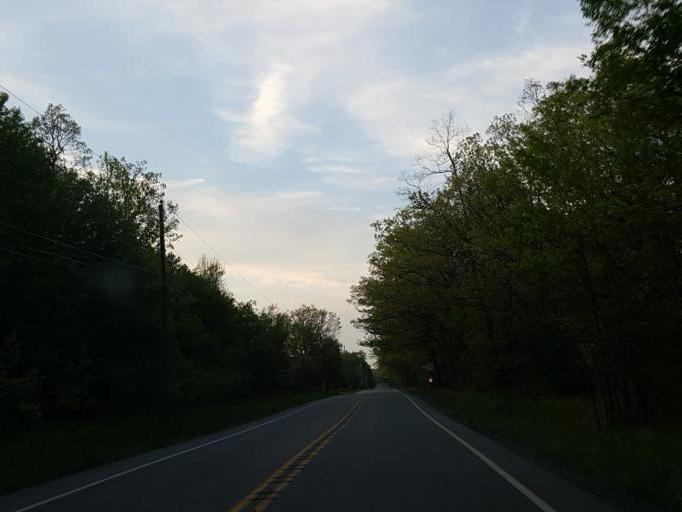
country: US
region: Pennsylvania
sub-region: Cambria County
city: Gallitzin
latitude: 40.5007
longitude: -78.5406
